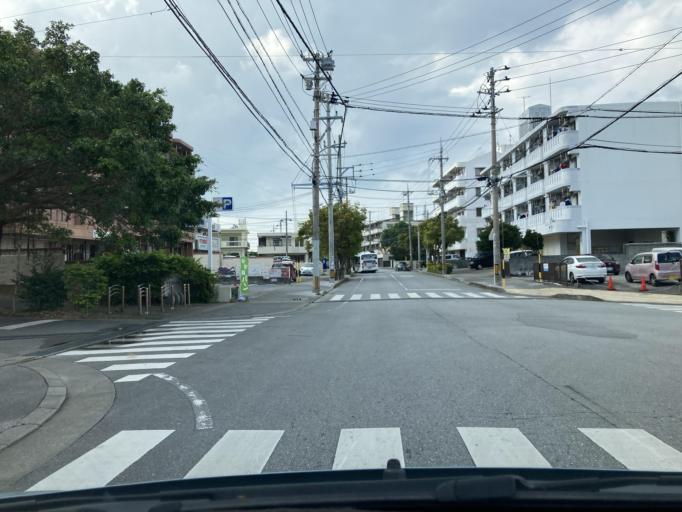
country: JP
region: Okinawa
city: Ginowan
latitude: 26.2421
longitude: 127.7626
